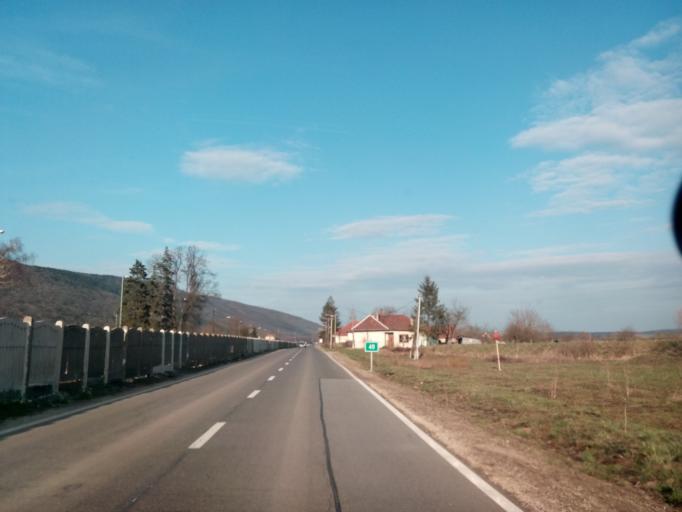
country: HU
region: Borsod-Abauj-Zemplen
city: Szendro
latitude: 48.5567
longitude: 20.7839
